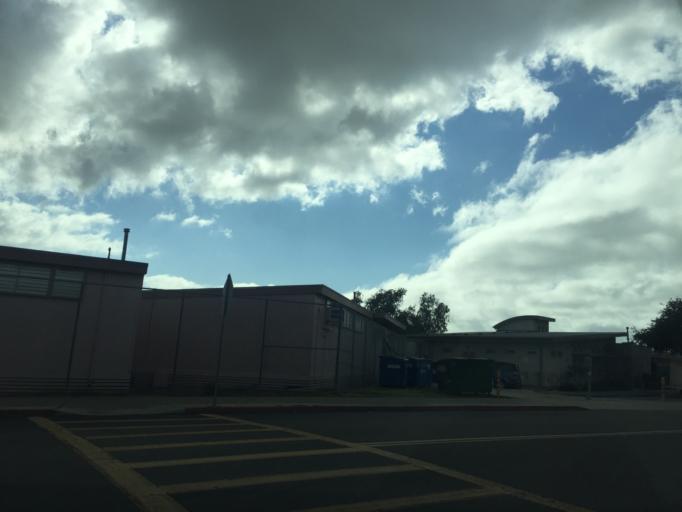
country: US
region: California
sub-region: San Diego County
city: La Jolla
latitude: 32.8031
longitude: -117.2244
